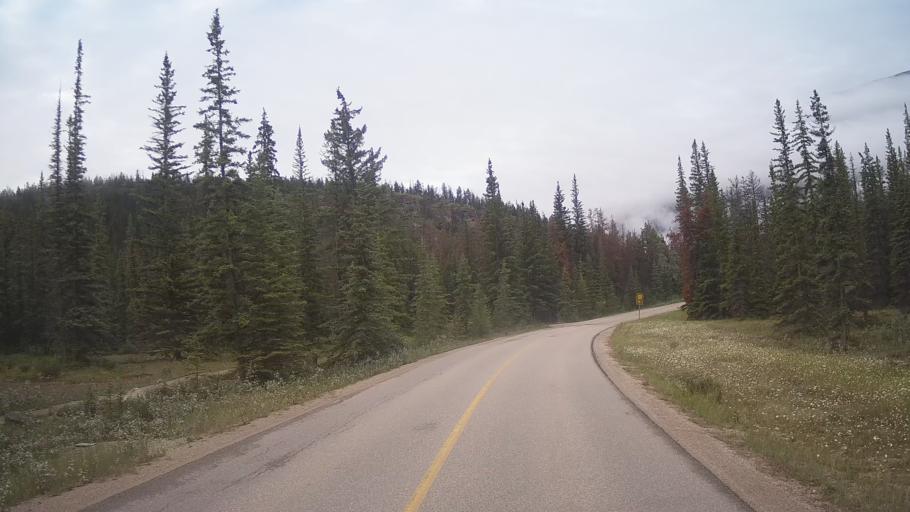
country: CA
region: Alberta
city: Jasper Park Lodge
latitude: 52.8626
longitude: -118.0704
